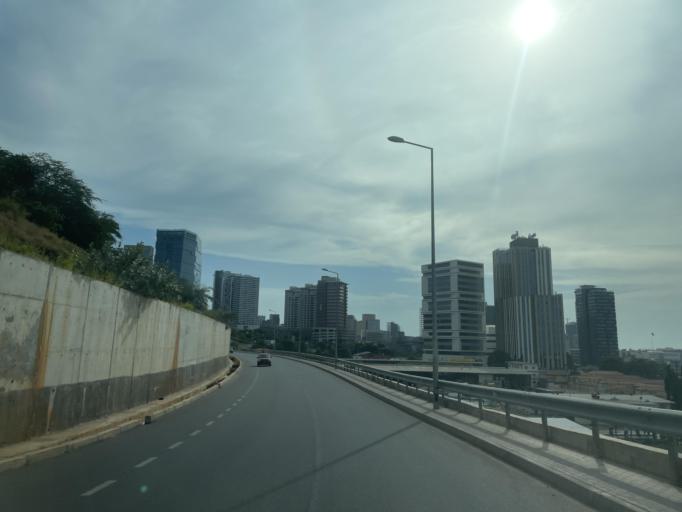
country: AO
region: Luanda
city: Luanda
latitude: -8.8074
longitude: 13.2459
